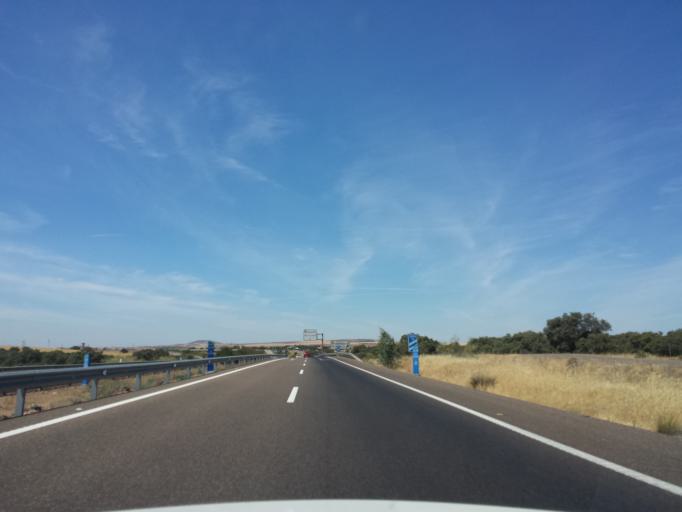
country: ES
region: Extremadura
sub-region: Provincia de Badajoz
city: Trujillanos
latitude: 38.9528
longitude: -6.2375
